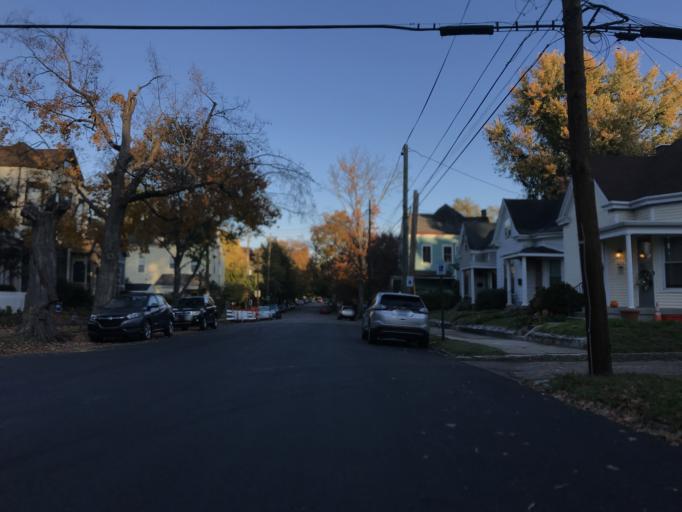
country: US
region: Kentucky
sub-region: Jefferson County
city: Audubon Park
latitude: 38.2380
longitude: -85.7270
